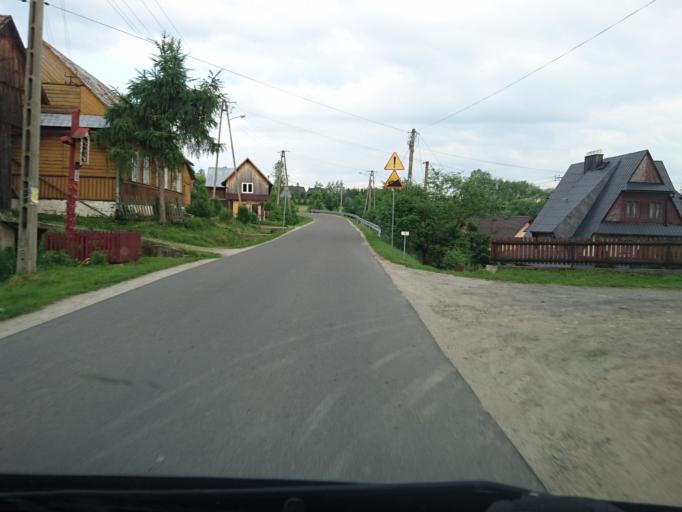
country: PL
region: Lesser Poland Voivodeship
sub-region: Powiat nowotarski
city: Frydman
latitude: 49.4804
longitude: 20.1866
